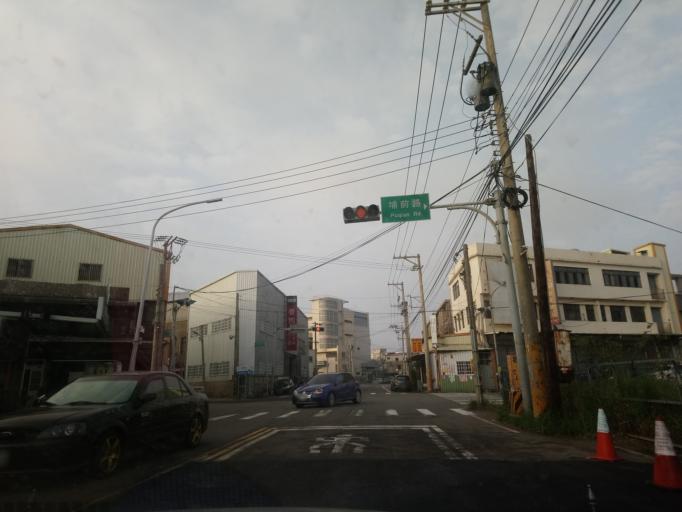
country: TW
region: Taiwan
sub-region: Hsinchu
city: Hsinchu
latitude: 24.7935
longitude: 120.9325
